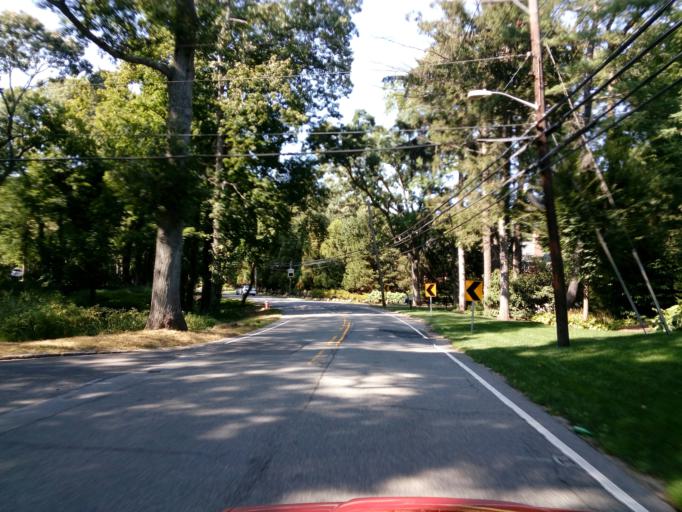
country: US
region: New York
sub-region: Nassau County
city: Muttontown
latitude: 40.8168
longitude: -73.5469
